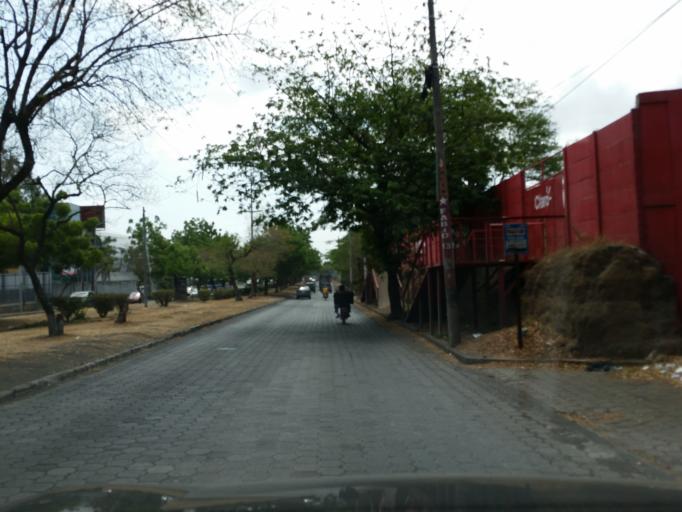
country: NI
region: Managua
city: Managua
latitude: 12.1125
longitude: -86.2634
